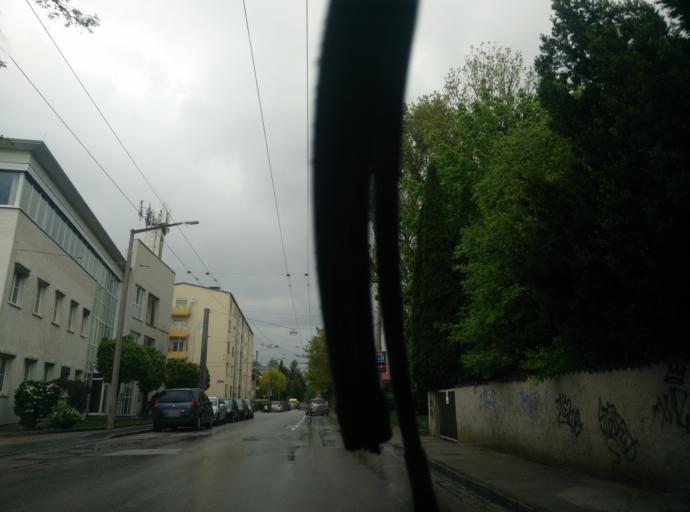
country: AT
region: Salzburg
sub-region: Politischer Bezirk Salzburg-Umgebung
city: Bergheim
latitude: 47.8214
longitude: 13.0268
